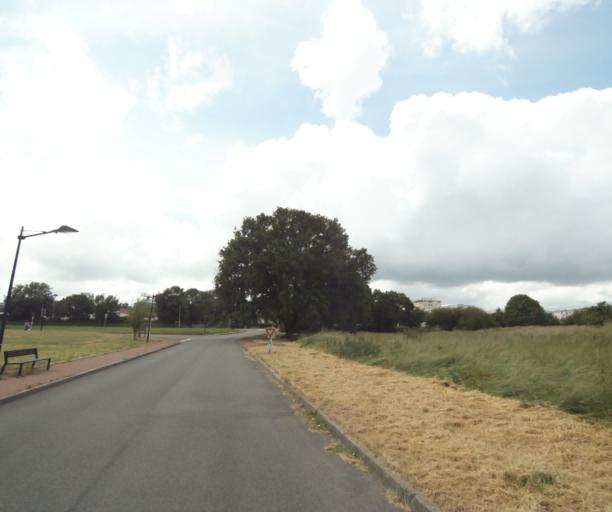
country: FR
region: Pays de la Loire
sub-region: Departement de la Sarthe
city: Solesmes
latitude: 47.8401
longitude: -0.3136
